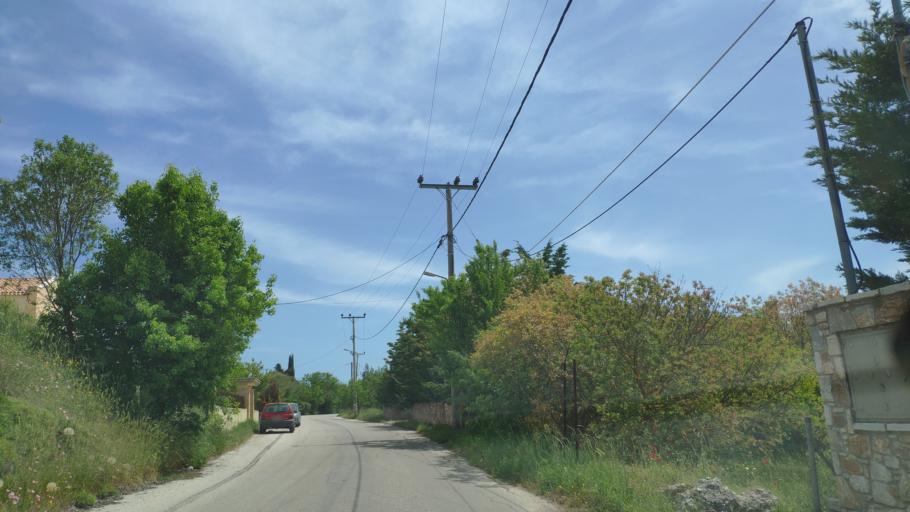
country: GR
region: Attica
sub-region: Nomarchia Anatolikis Attikis
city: Varnavas
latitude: 38.2310
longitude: 23.9375
